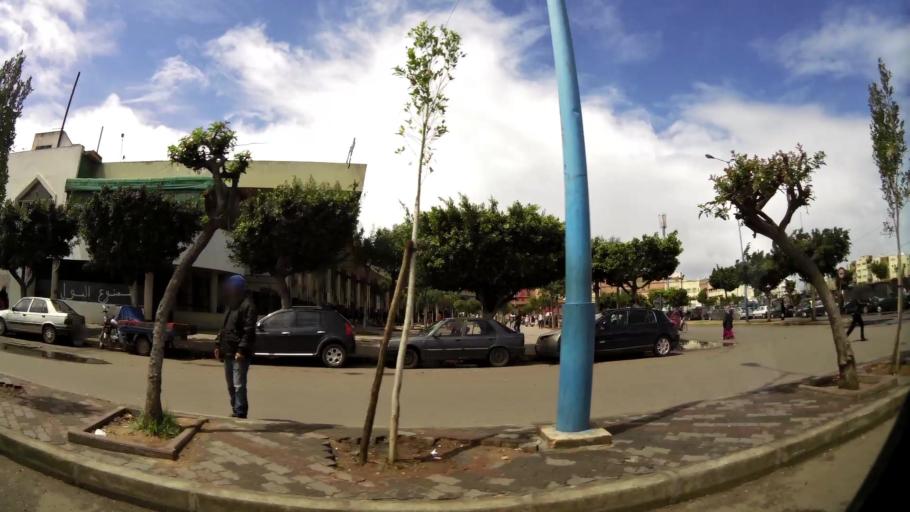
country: MA
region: Grand Casablanca
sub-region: Casablanca
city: Casablanca
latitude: 33.5752
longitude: -7.5876
